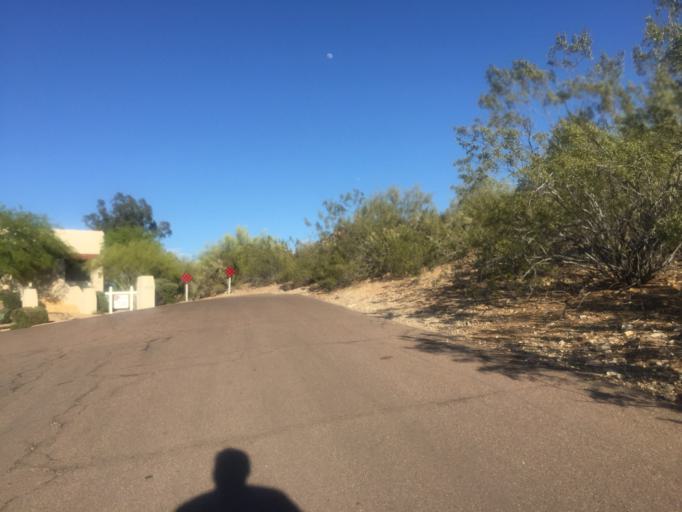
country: US
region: Arizona
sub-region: Maricopa County
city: Paradise Valley
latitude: 33.5755
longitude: -111.9997
